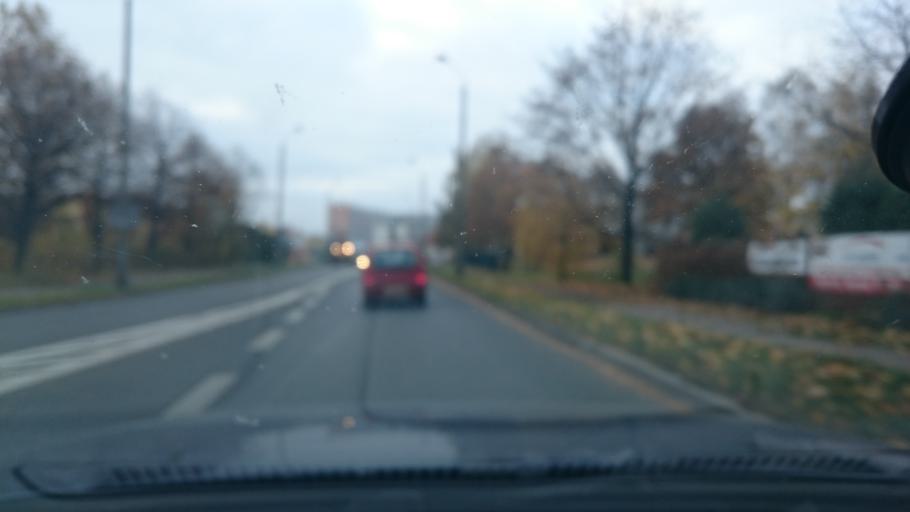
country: PL
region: Silesian Voivodeship
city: Zebrzydowice
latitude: 50.0970
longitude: 18.5147
